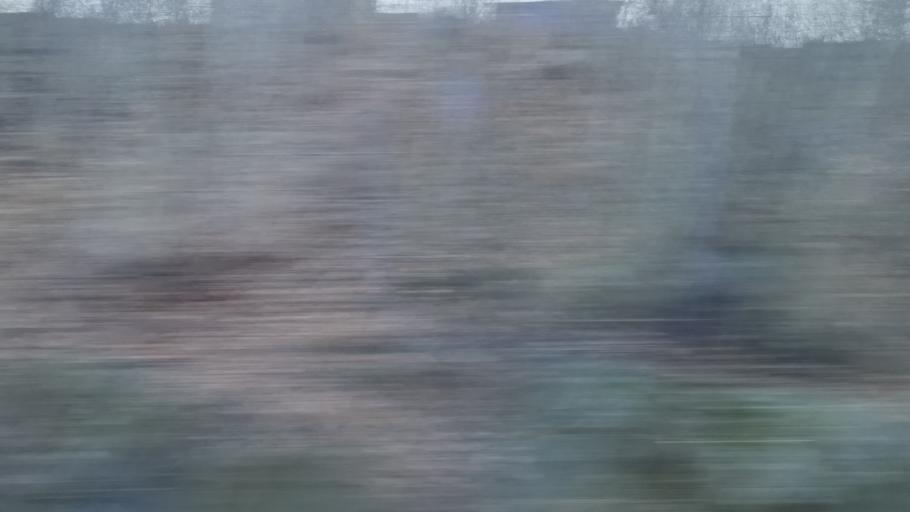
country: SE
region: Stockholm
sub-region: Sodertalje Kommun
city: Molnbo
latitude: 59.0483
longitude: 17.4223
